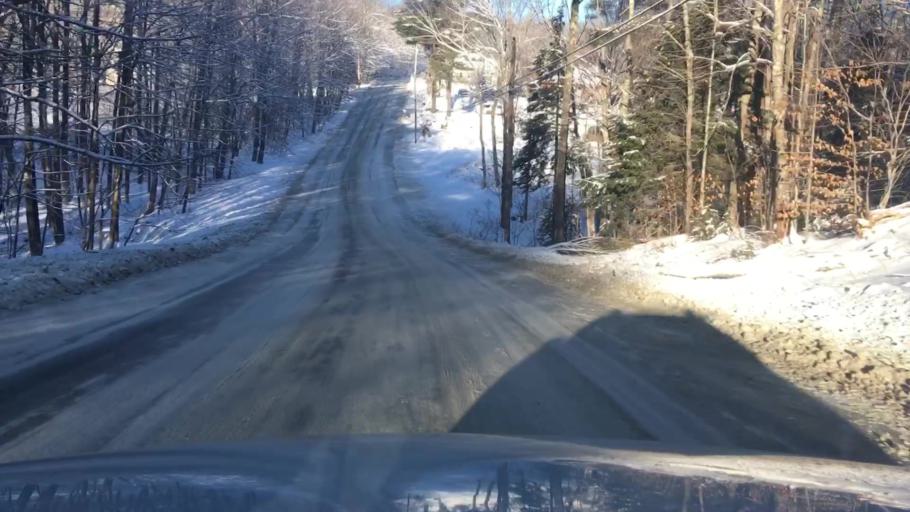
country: US
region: Maine
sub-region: Kennebec County
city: Readfield
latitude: 44.4185
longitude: -69.9233
